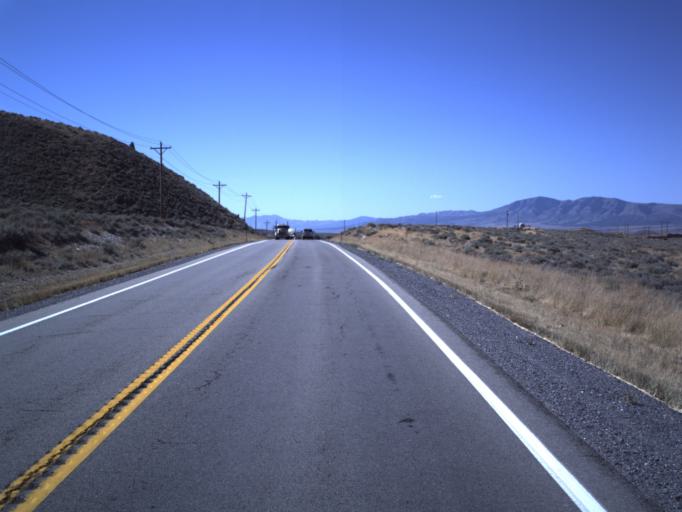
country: US
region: Utah
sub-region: Tooele County
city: Tooele
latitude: 40.4704
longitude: -112.3511
